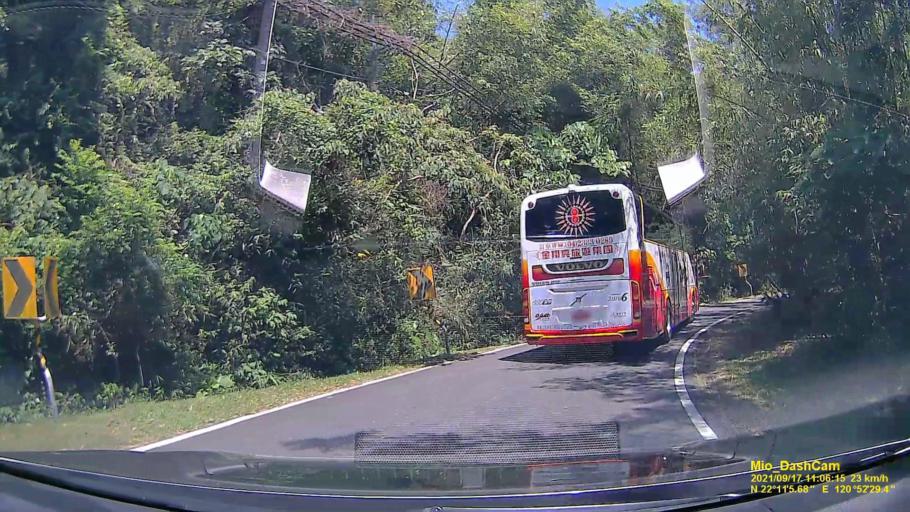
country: TW
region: Taiwan
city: Hengchun
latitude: 22.1850
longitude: 120.8748
